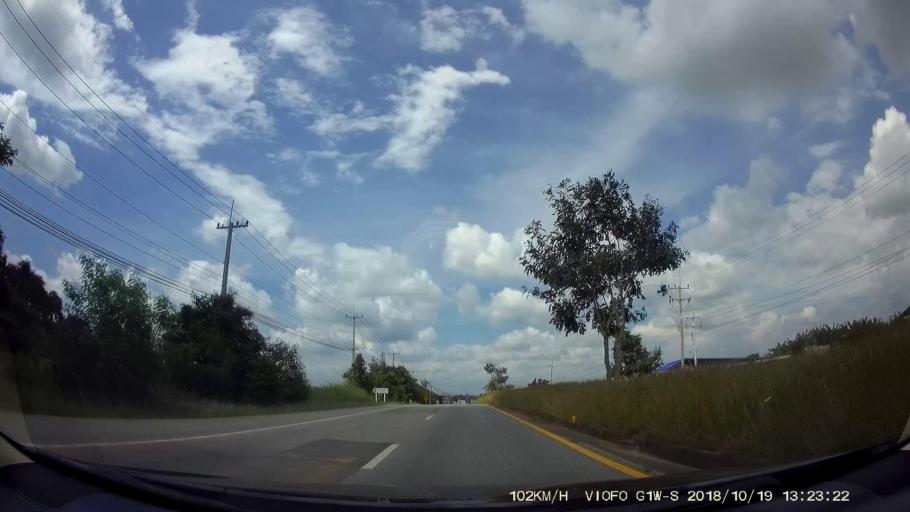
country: TH
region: Chaiyaphum
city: Chatturat
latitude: 15.4908
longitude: 101.8217
